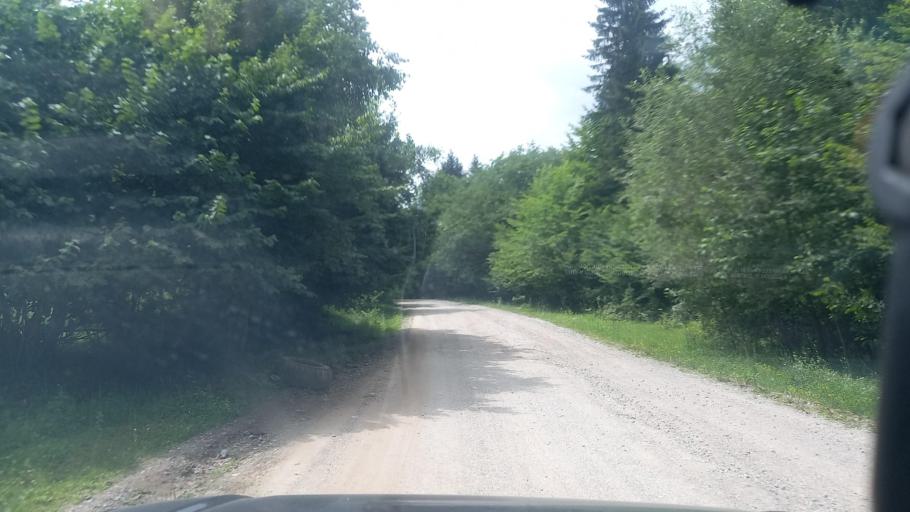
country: RU
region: Karachayevo-Cherkesiya
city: Kurdzhinovo
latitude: 43.8338
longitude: 40.9260
